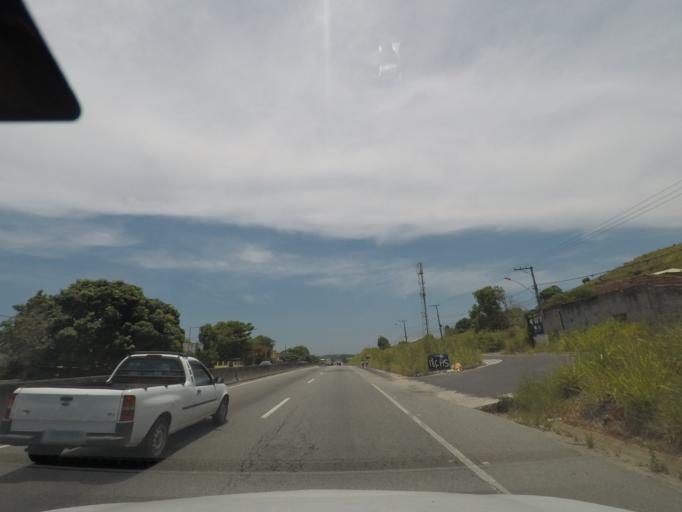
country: BR
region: Rio de Janeiro
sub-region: Marica
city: Marica
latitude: -22.9213
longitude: -42.8577
